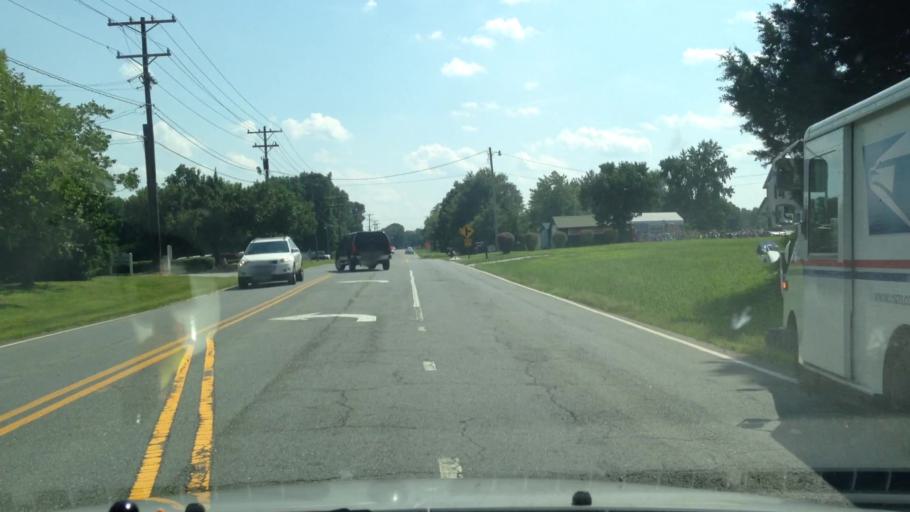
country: US
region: North Carolina
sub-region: Forsyth County
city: Kernersville
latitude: 36.1403
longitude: -80.0498
